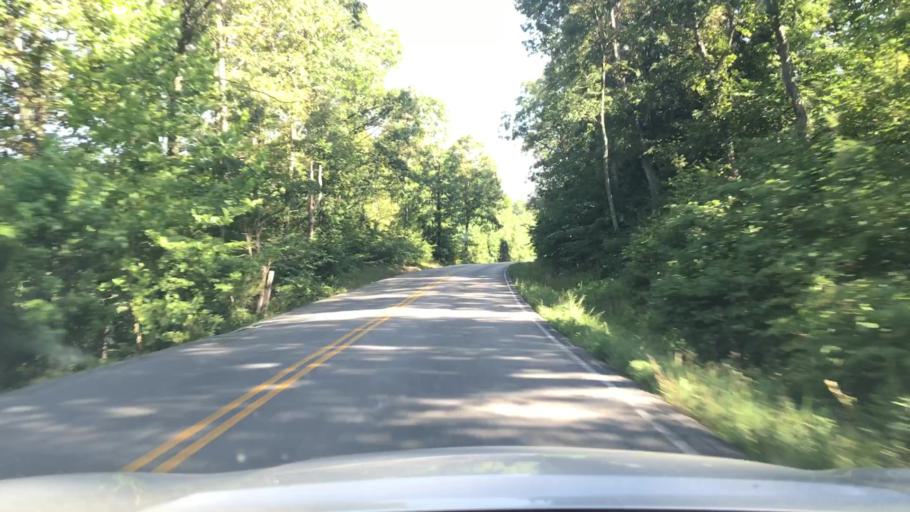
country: US
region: Kentucky
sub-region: Muhlenberg County
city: Greenville
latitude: 37.1350
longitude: -87.1432
